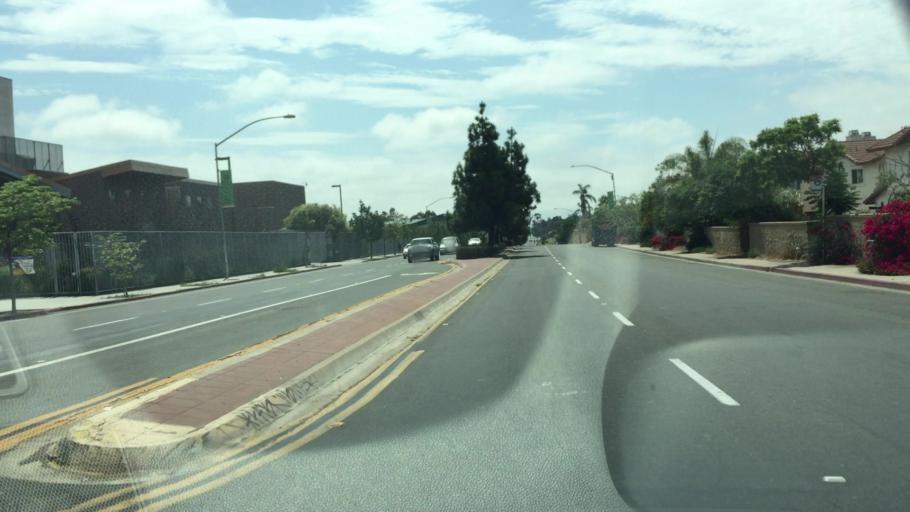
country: US
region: California
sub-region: San Diego County
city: National City
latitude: 32.7042
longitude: -117.0896
